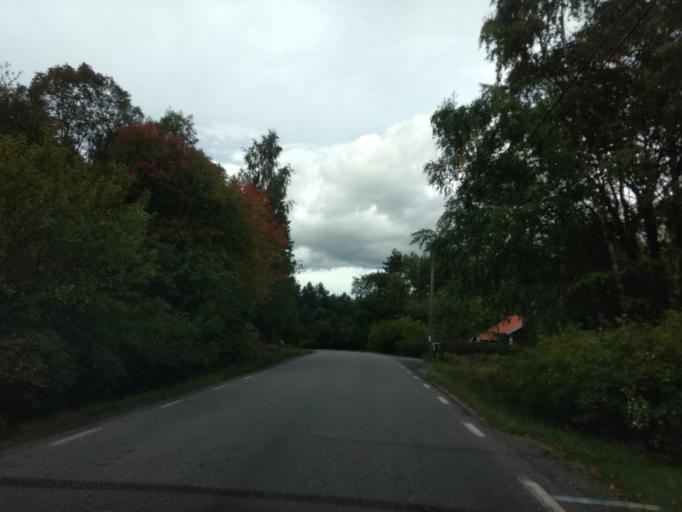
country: SE
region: Uppsala
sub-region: Habo Kommun
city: Balsta
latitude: 59.6979
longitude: 17.5379
